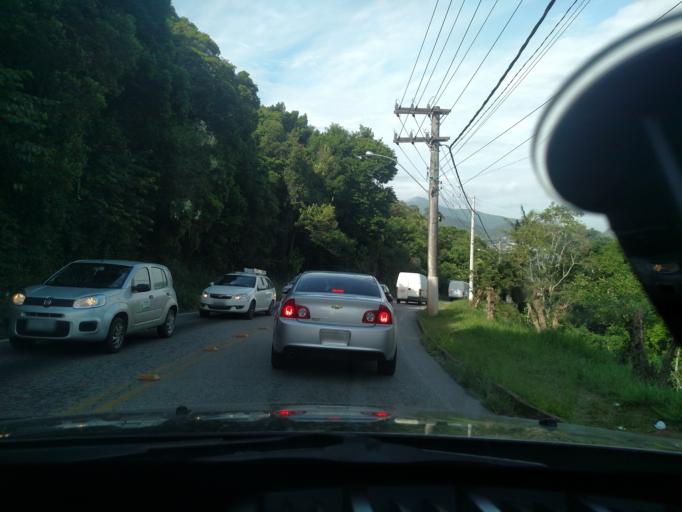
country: BR
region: Santa Catarina
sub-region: Porto Belo
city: Porto Belo
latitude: -27.1422
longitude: -48.5262
